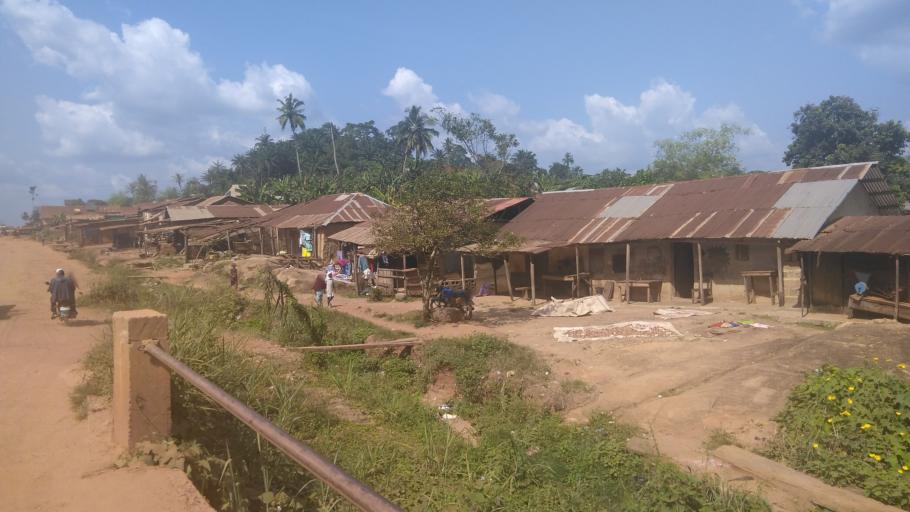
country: NG
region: Osun
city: Ifetedo
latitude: 7.0150
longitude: 4.6336
